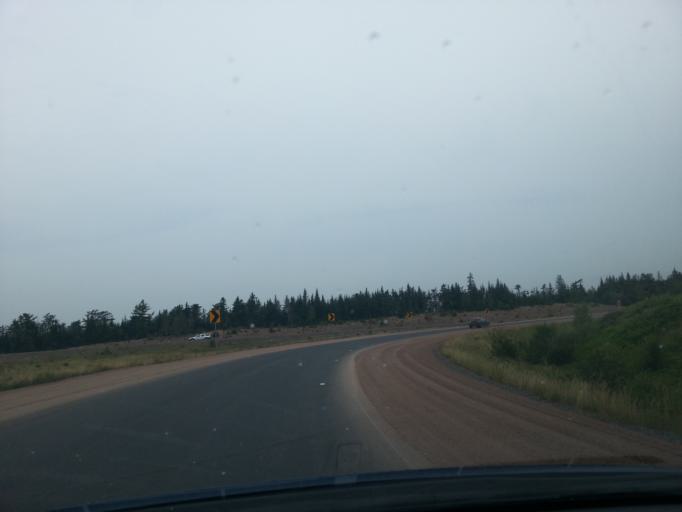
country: CA
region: Nova Scotia
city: Truro
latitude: 45.4105
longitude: -63.5335
